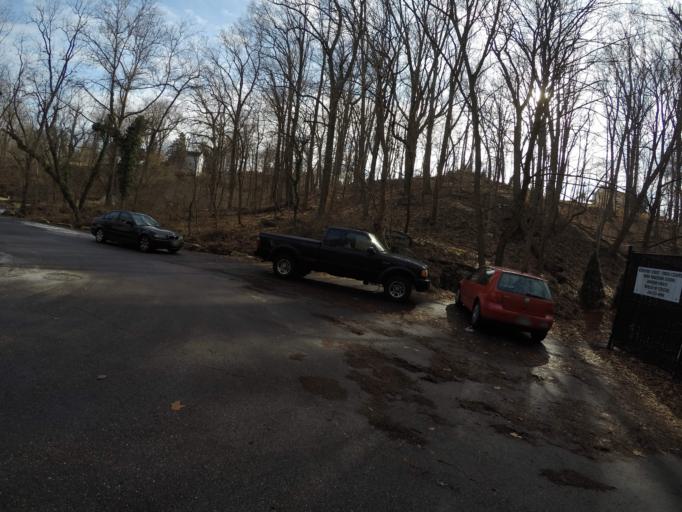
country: US
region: Maryland
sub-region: Howard County
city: Ellicott City
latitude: 39.2669
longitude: -76.8021
